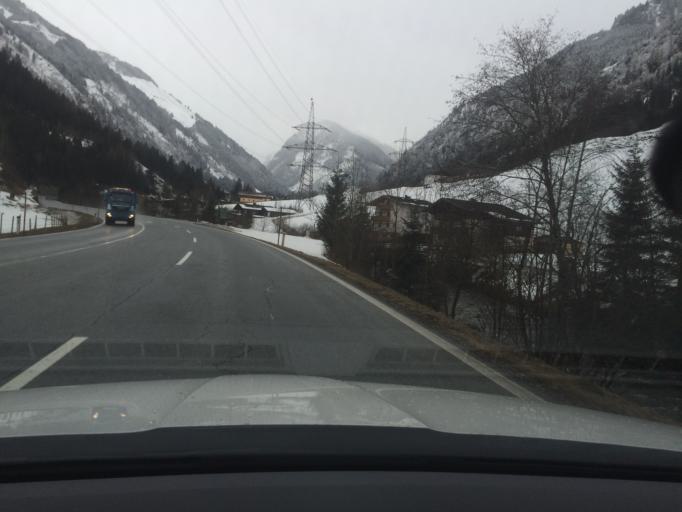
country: AT
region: Salzburg
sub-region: Politischer Bezirk Zell am See
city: Mittersill
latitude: 47.2531
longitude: 12.4860
